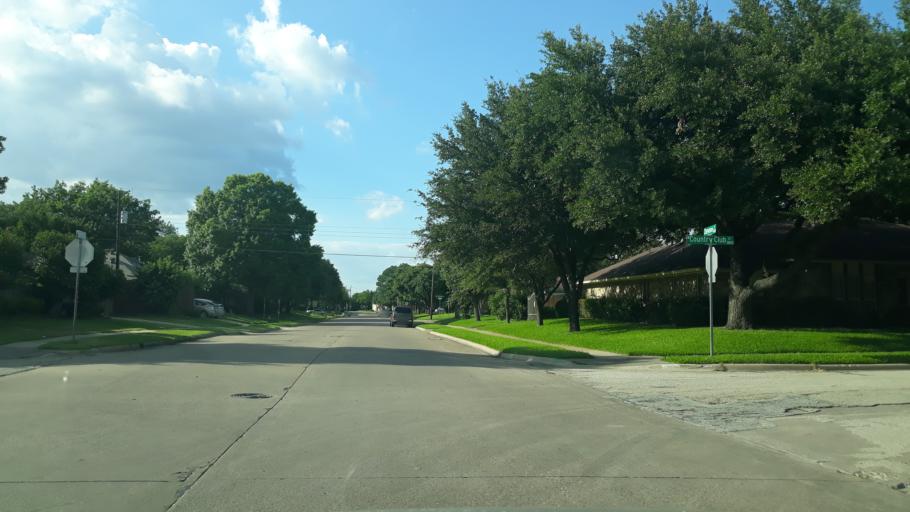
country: US
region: Texas
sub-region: Dallas County
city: Irving
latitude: 32.8598
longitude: -97.0020
